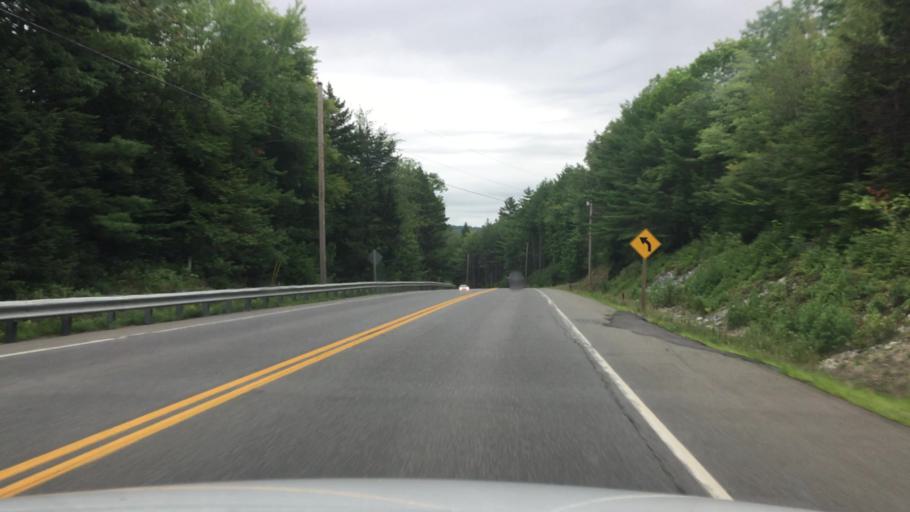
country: US
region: Maine
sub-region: Penobscot County
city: Bradley
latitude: 44.8254
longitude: -68.4108
